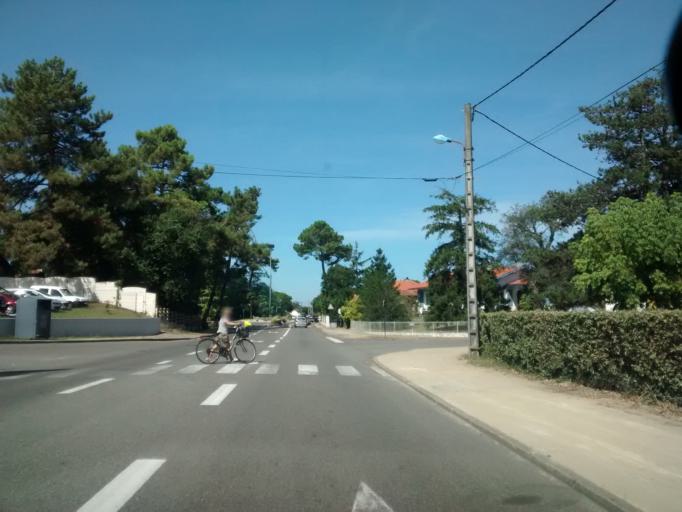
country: FR
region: Aquitaine
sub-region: Departement des Landes
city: Capbreton
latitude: 43.6365
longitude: -1.4201
